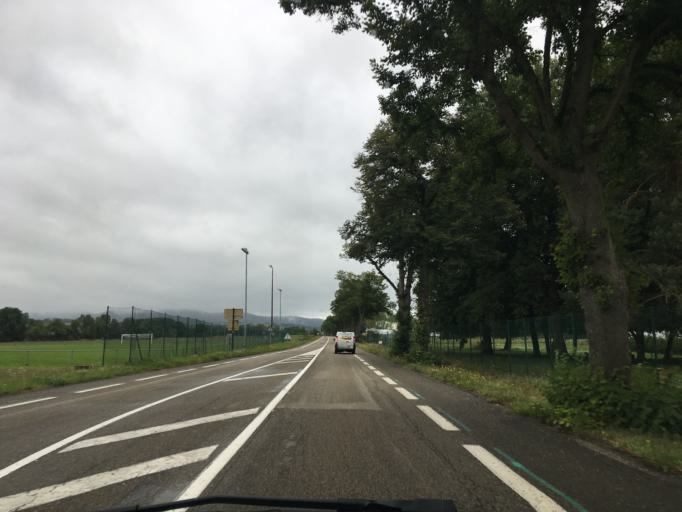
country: DE
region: Rheinland-Pfalz
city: Schweighofen
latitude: 49.0222
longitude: 7.9873
